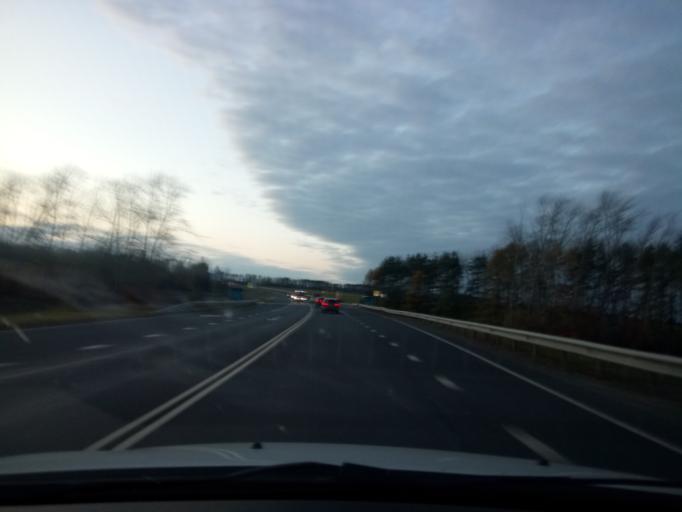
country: RU
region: Nizjnij Novgorod
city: Bol'shoye Murashkino
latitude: 55.8878
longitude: 44.7455
